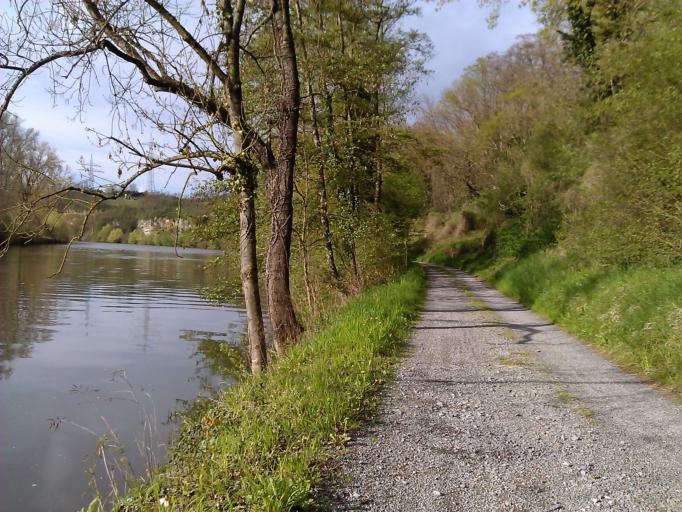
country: DE
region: Baden-Wuerttemberg
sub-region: Regierungsbezirk Stuttgart
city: Talheim
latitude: 49.0824
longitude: 9.1778
